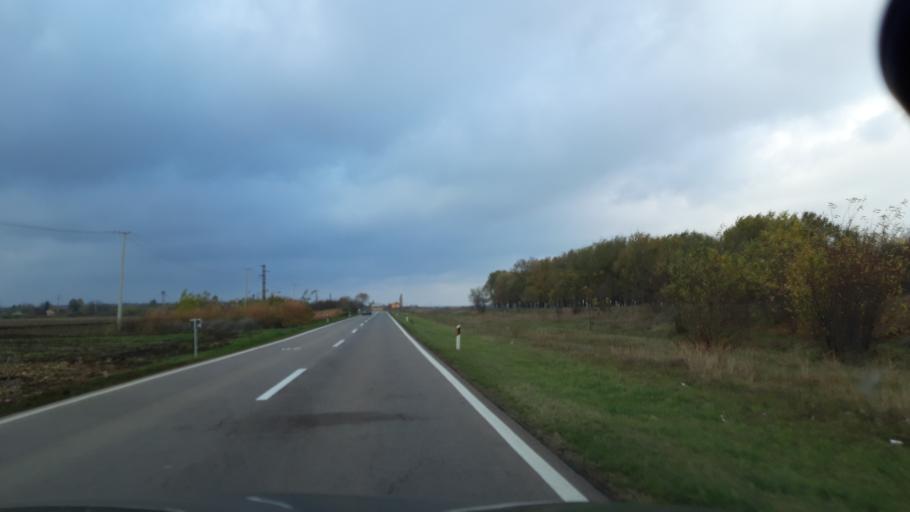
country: RS
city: Sanad
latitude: 45.9729
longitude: 20.1208
